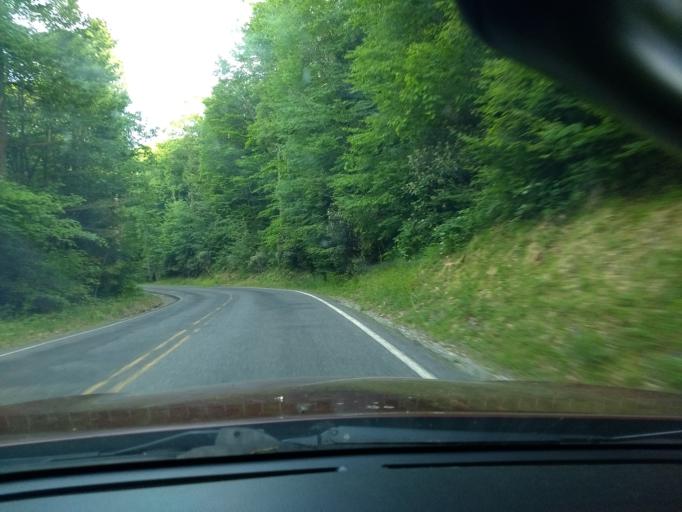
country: US
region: Pennsylvania
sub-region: Cambria County
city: Gallitzin
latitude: 40.5004
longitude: -78.5126
